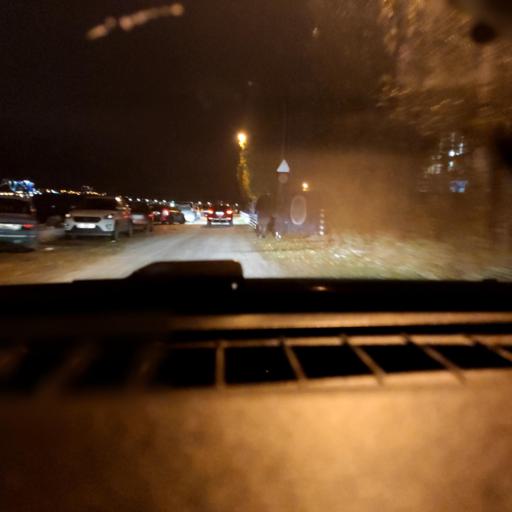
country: RU
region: Voronezj
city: Voronezh
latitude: 51.6756
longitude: 39.2424
